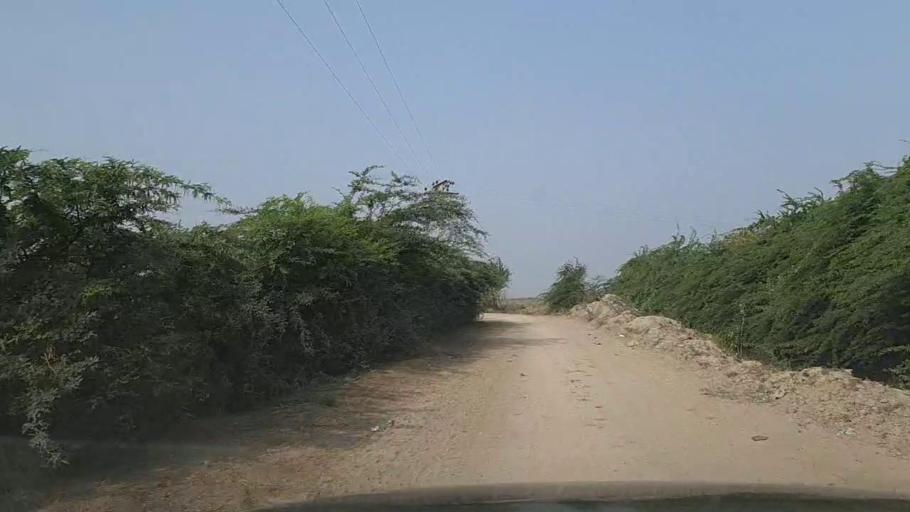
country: PK
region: Sindh
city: Thatta
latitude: 24.7682
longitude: 67.8600
